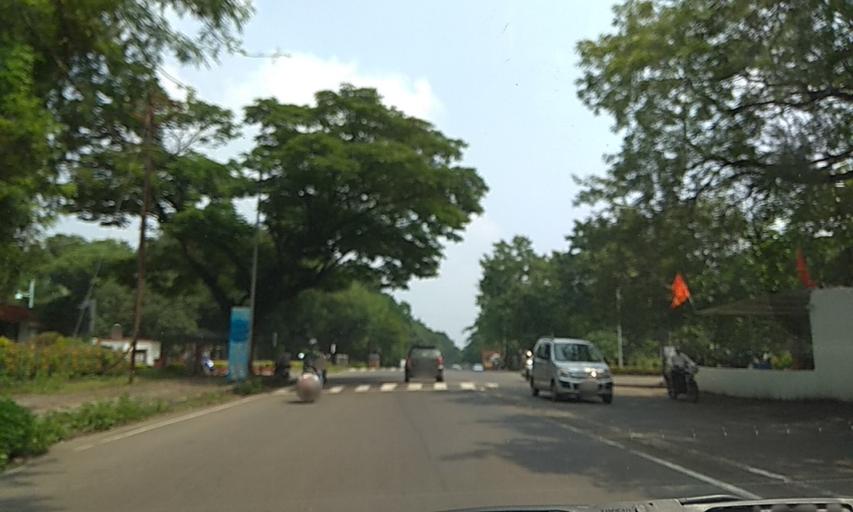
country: IN
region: Maharashtra
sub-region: Pune Division
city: Shivaji Nagar
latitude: 18.5395
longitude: 73.8112
